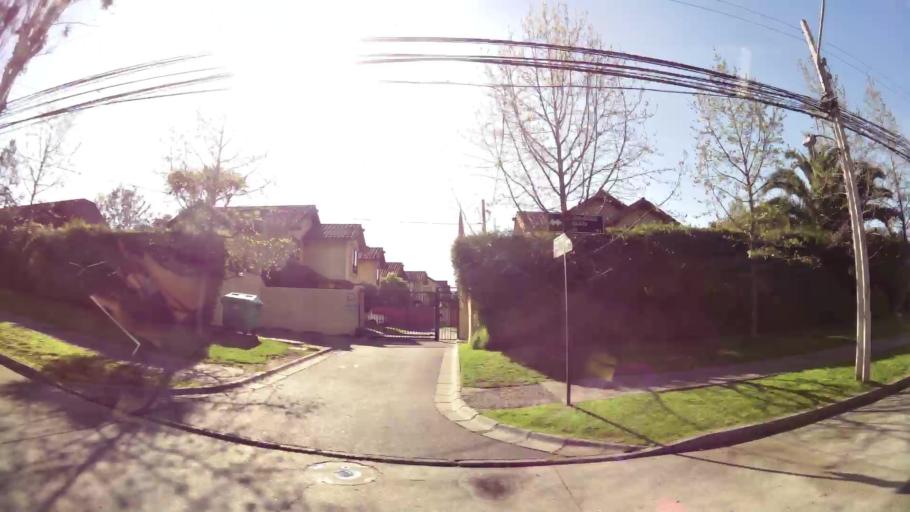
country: CL
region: Santiago Metropolitan
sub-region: Provincia de Santiago
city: Villa Presidente Frei, Nunoa, Santiago, Chile
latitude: -33.4472
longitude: -70.5514
